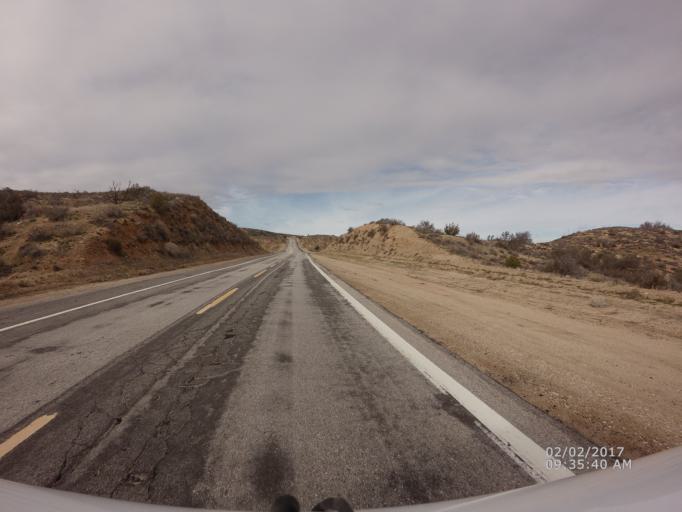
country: US
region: California
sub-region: Los Angeles County
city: Vincent
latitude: 34.5029
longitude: -118.0544
